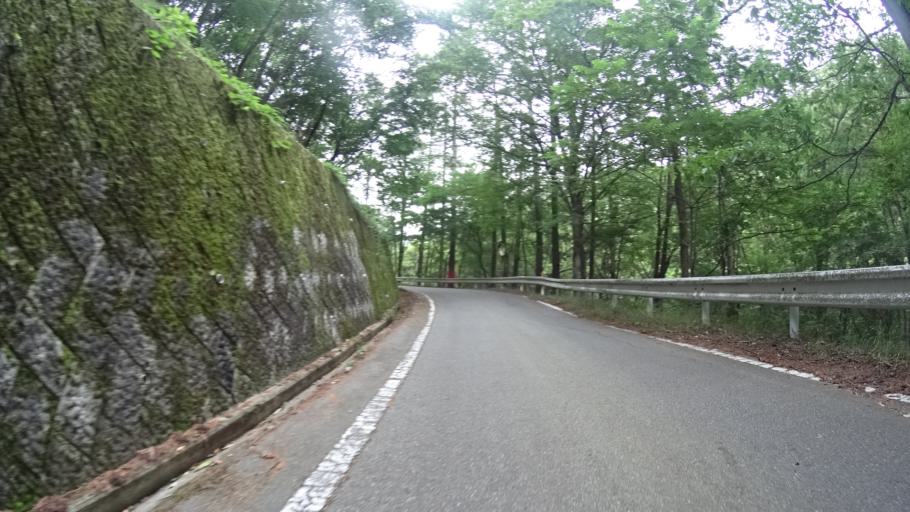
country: JP
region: Yamanashi
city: Kofu-shi
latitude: 35.8563
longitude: 138.5712
